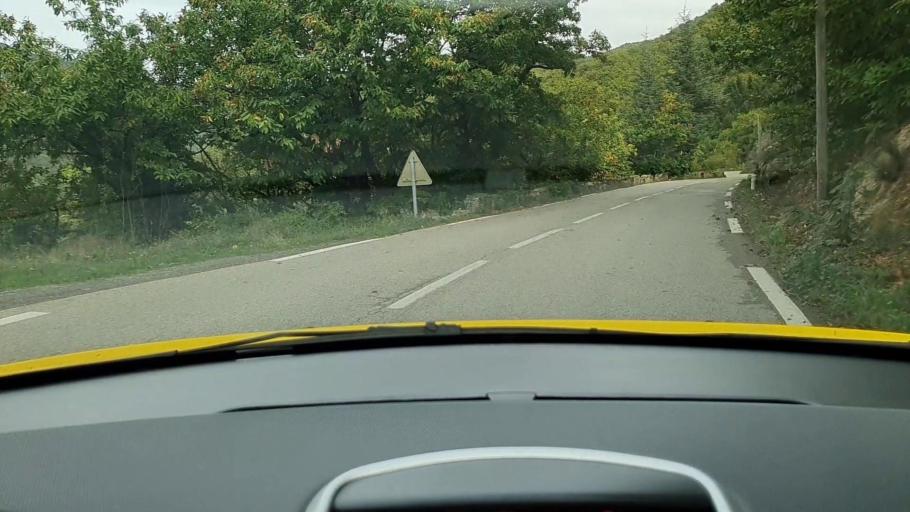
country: FR
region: Languedoc-Roussillon
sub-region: Departement du Gard
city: Le Vigan
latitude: 44.0226
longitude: 3.5966
